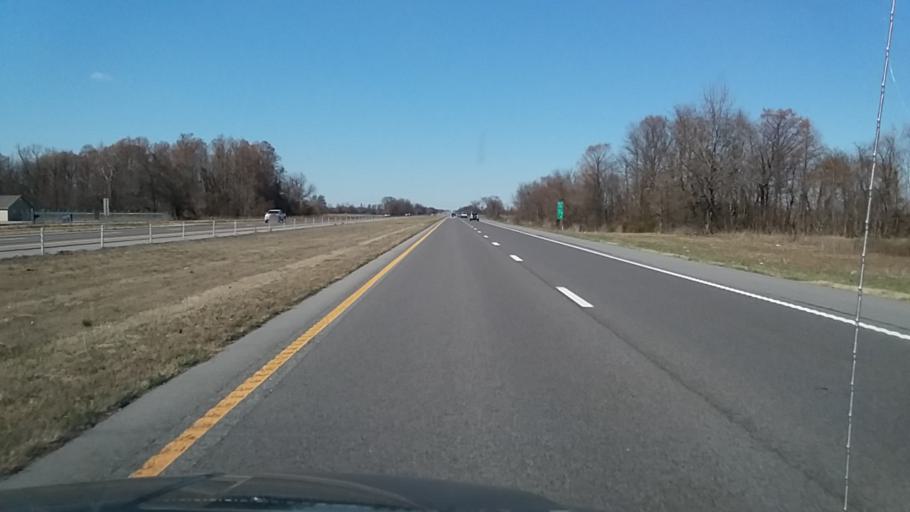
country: US
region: Missouri
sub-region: Scott County
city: Sikeston
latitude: 36.9785
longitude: -89.5345
